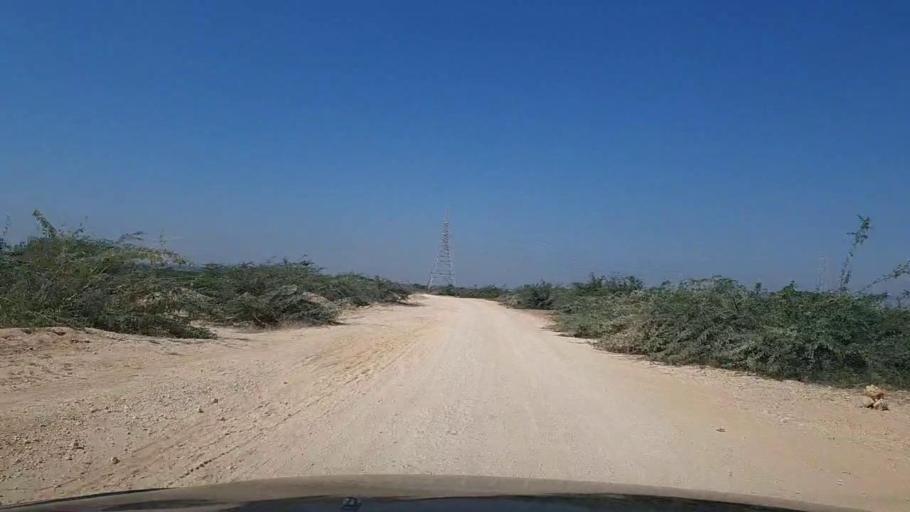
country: PK
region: Sindh
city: Thatta
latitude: 24.6238
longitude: 67.8377
